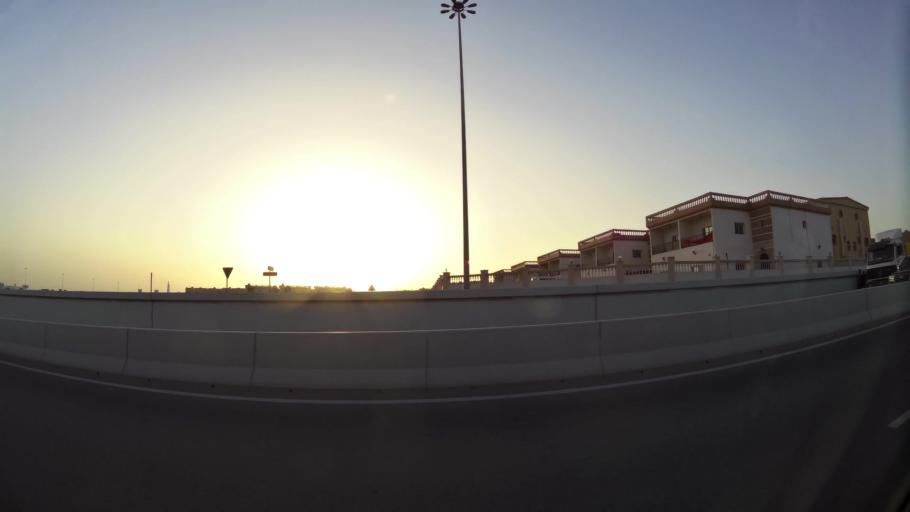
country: QA
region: Baladiyat ar Rayyan
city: Ar Rayyan
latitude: 25.3230
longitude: 51.4607
